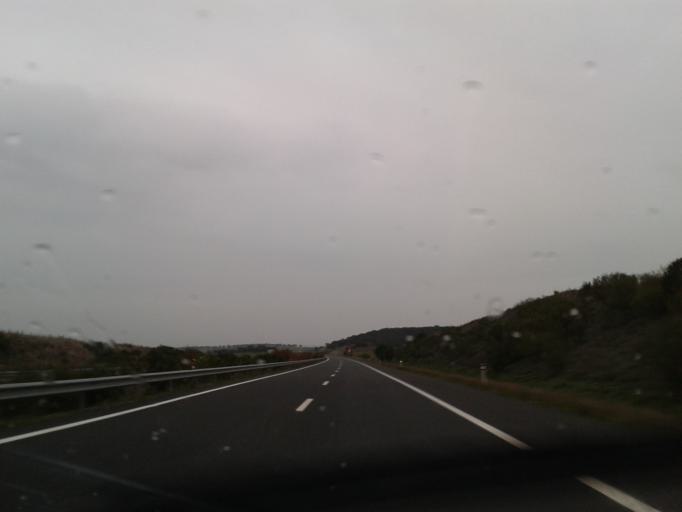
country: PT
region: Beja
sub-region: Aljustrel
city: Aljustrel
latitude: 37.8641
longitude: -8.2309
